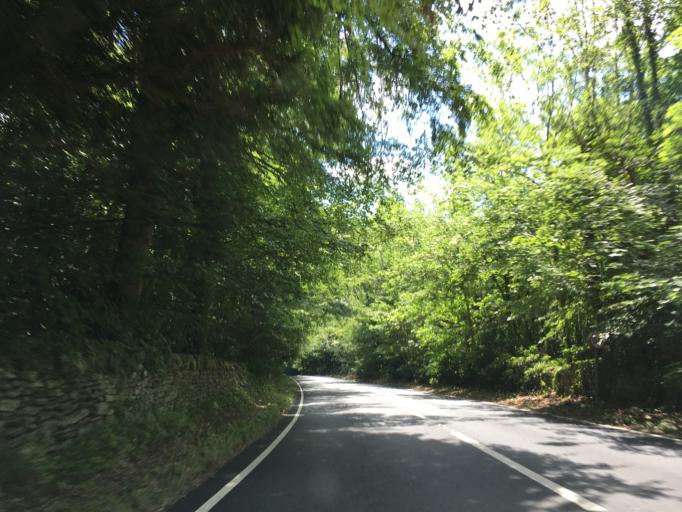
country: GB
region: England
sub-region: Gloucestershire
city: Painswick
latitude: 51.7960
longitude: -2.1955
